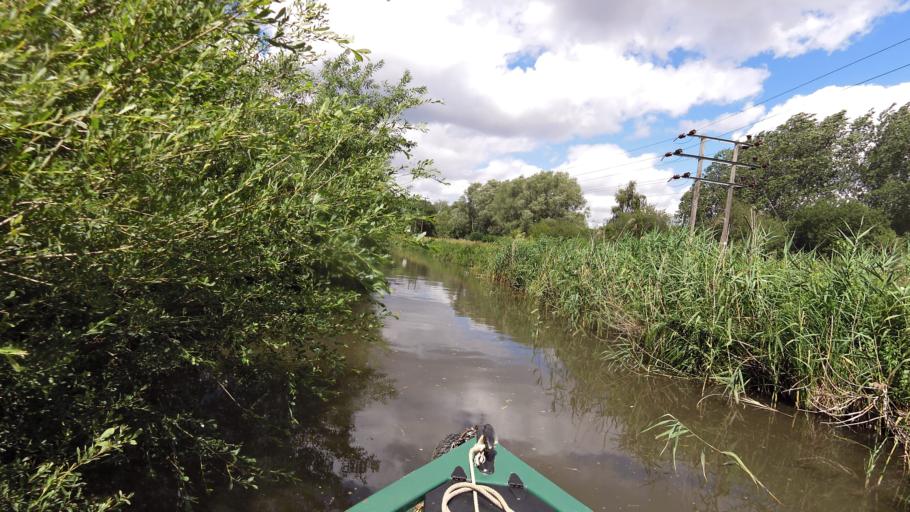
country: GB
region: England
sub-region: West Berkshire
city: Greenham
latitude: 51.3992
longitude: -1.2889
